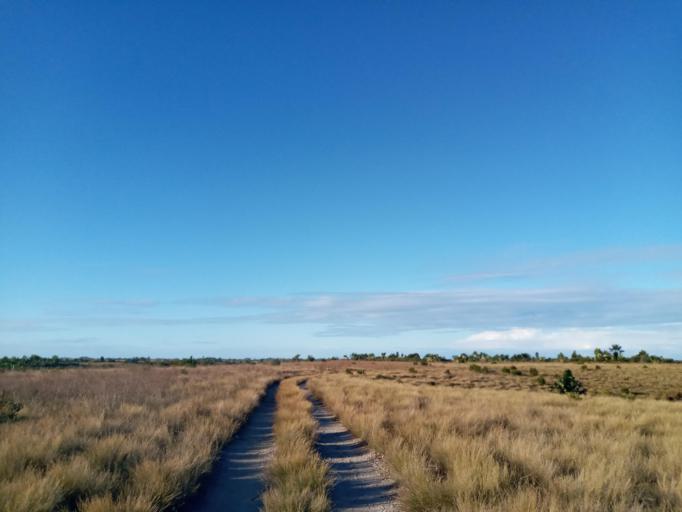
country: MG
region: Anosy
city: Fort Dauphin
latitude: -24.4307
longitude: 47.2946
